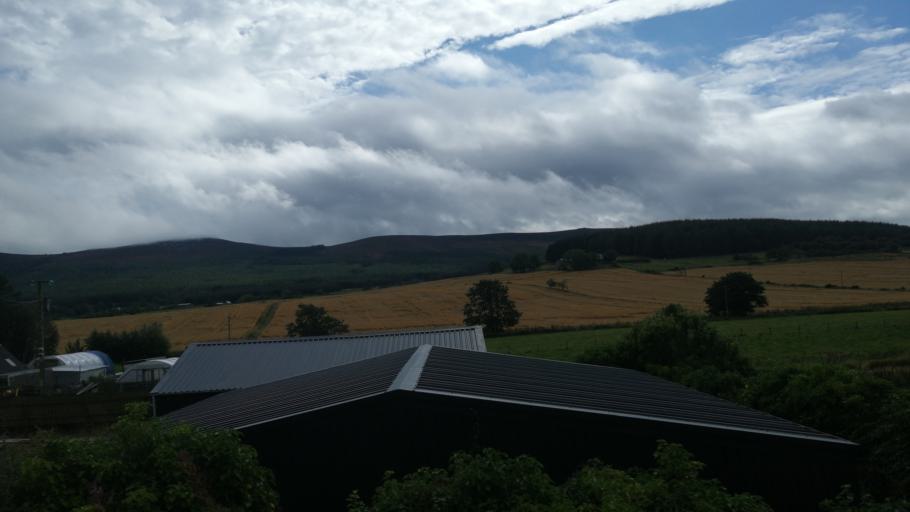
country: GB
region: Scotland
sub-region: Aberdeenshire
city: Insch
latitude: 57.3242
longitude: -2.5673
